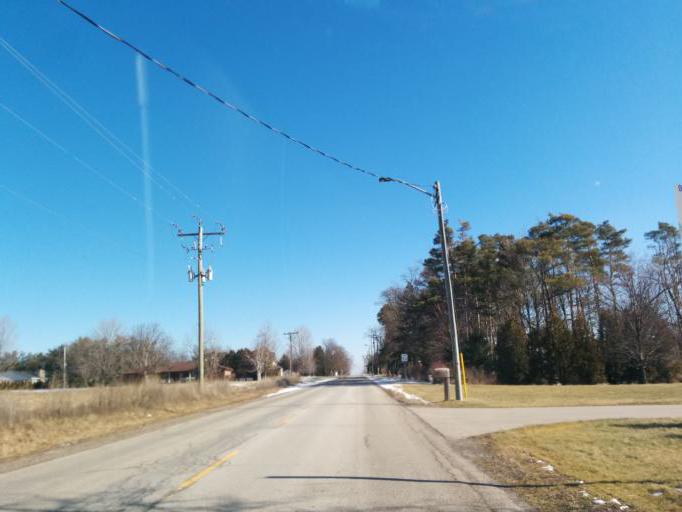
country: CA
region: Ontario
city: Brant
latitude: 43.0218
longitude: -80.3830
